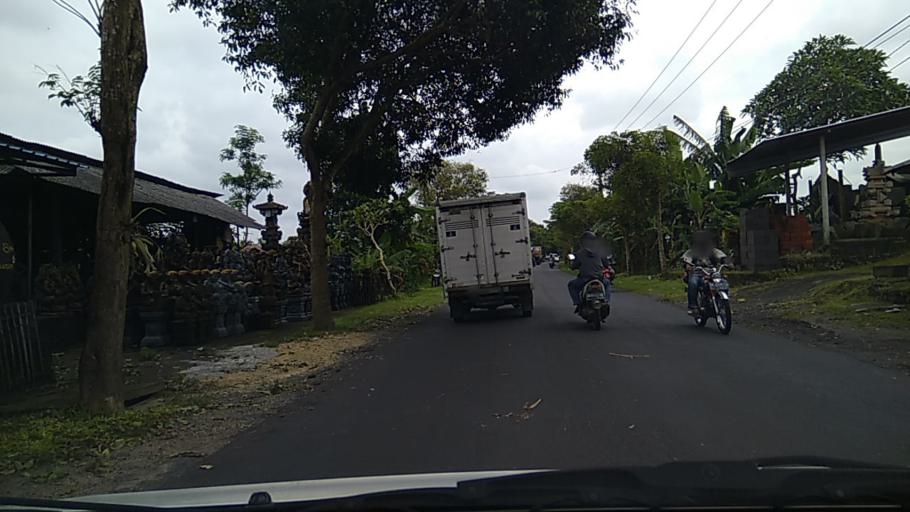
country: ID
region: Bali
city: Banjar Kembangsari
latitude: -8.5009
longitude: 115.2101
